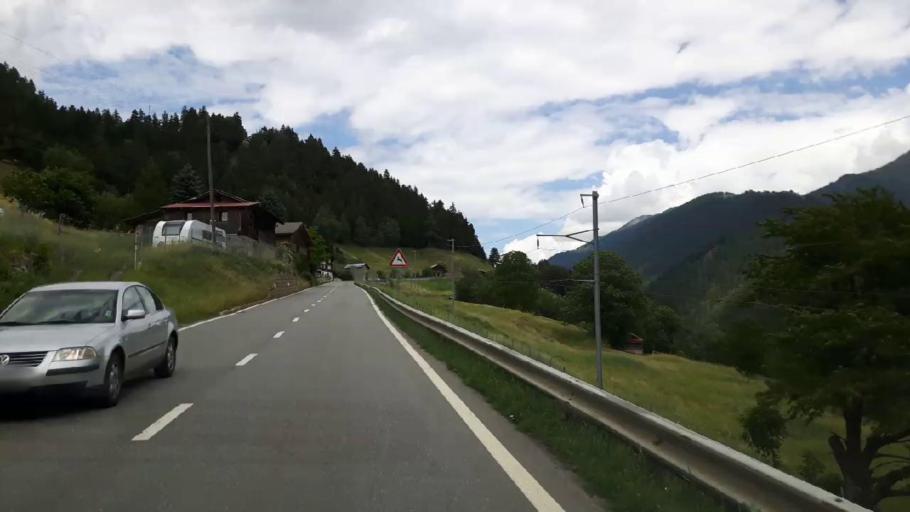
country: CH
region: Valais
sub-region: Goms District
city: Fiesch
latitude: 46.3788
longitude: 8.1023
